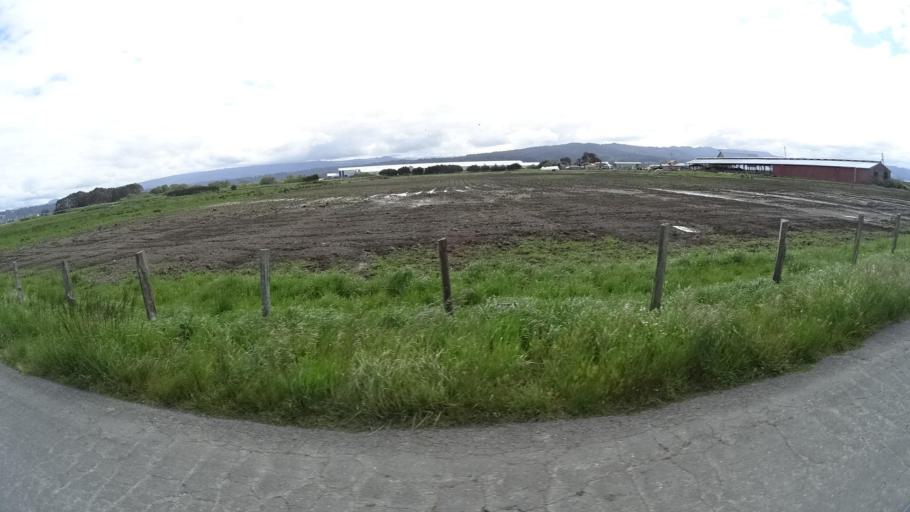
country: US
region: California
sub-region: Humboldt County
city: Arcata
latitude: 40.8846
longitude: -124.1158
